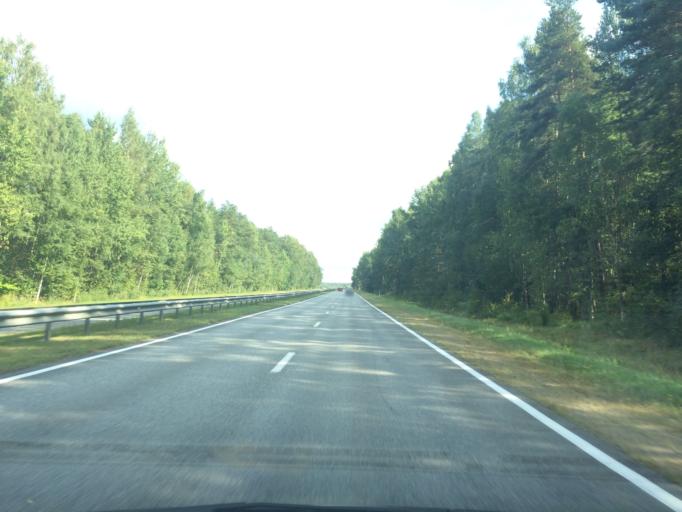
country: LV
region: Ikskile
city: Ikskile
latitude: 56.8267
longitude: 24.5244
